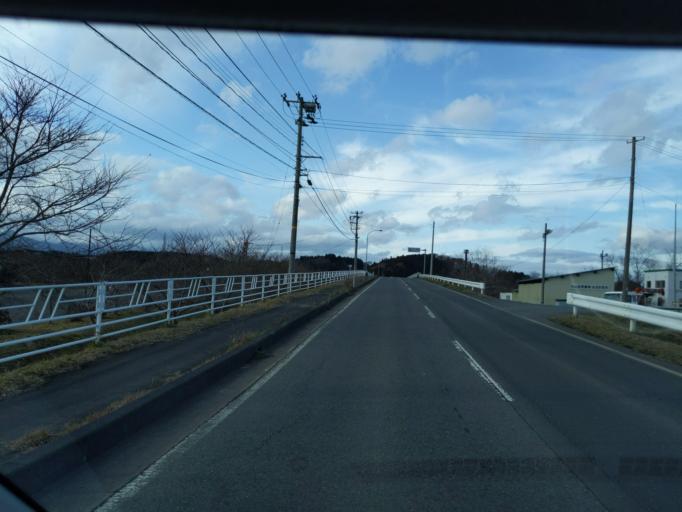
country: JP
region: Iwate
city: Mizusawa
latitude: 39.1645
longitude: 141.0918
